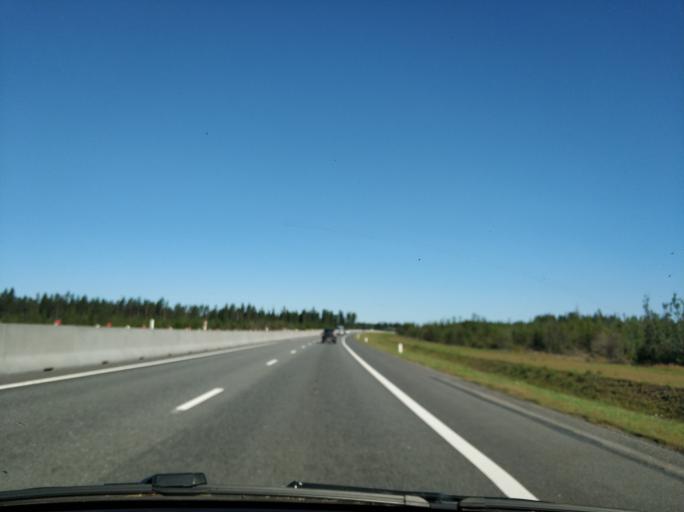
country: RU
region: Leningrad
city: Sosnovo
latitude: 60.4396
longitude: 30.2157
